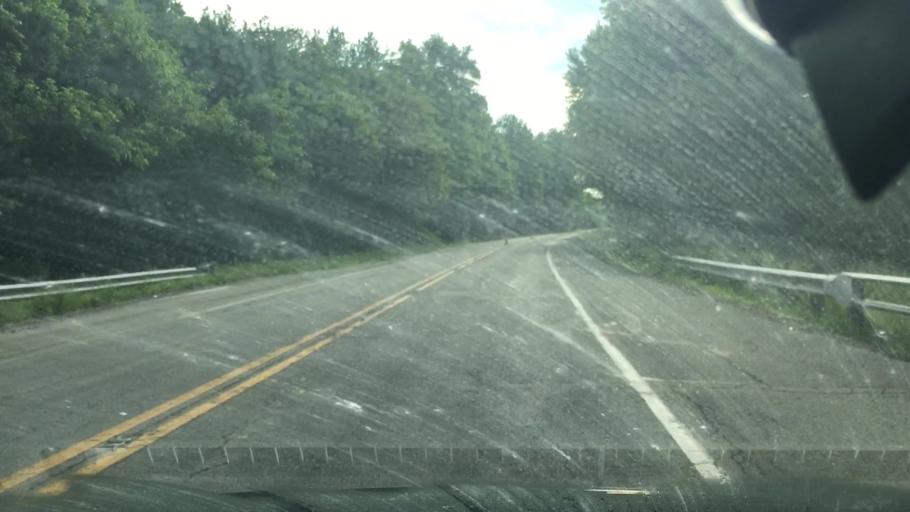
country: US
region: Kentucky
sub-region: Hancock County
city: Lewisport
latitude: 37.9503
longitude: -86.9613
